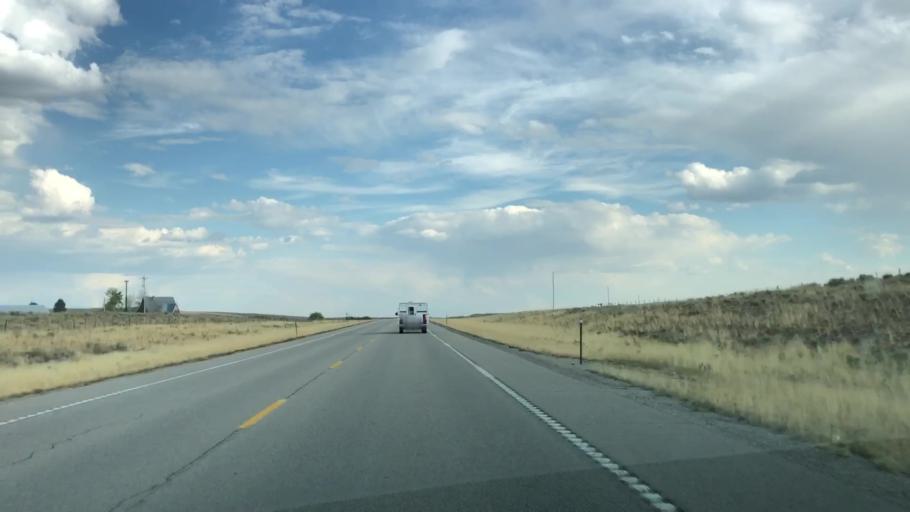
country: US
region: Wyoming
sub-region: Sublette County
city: Pinedale
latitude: 43.0174
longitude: -110.1172
